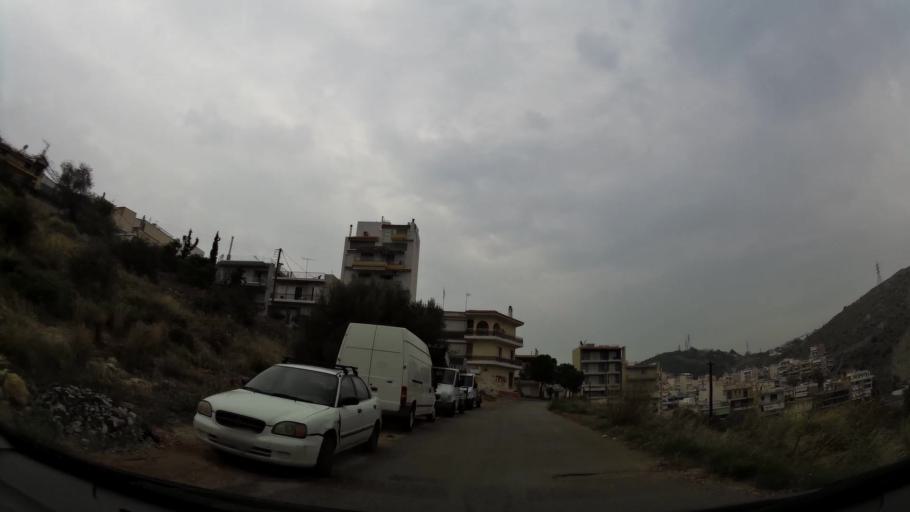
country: GR
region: Attica
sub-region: Nomos Piraios
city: Korydallos
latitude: 37.9933
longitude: 23.6411
